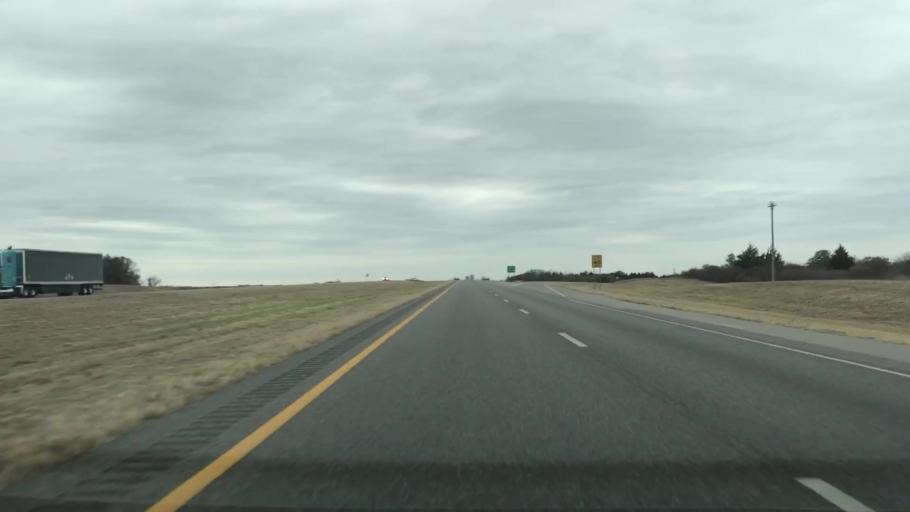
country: US
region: Oklahoma
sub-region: Beckham County
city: Erick
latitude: 35.2266
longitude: -99.9069
